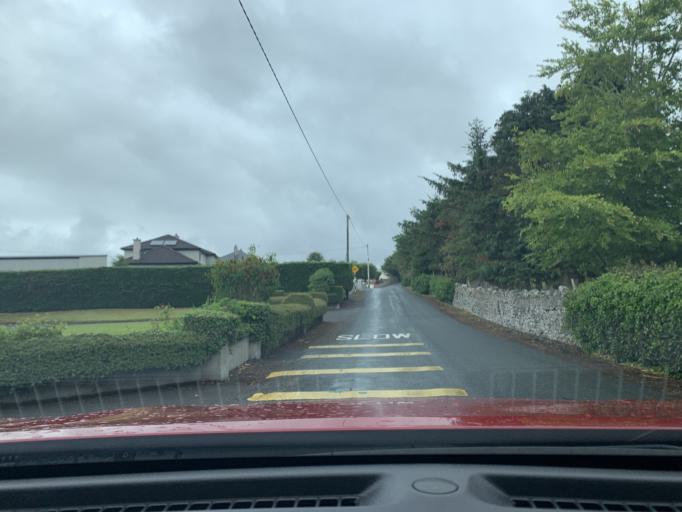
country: IE
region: Connaught
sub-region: Sligo
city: Sligo
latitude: 54.2963
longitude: -8.4613
